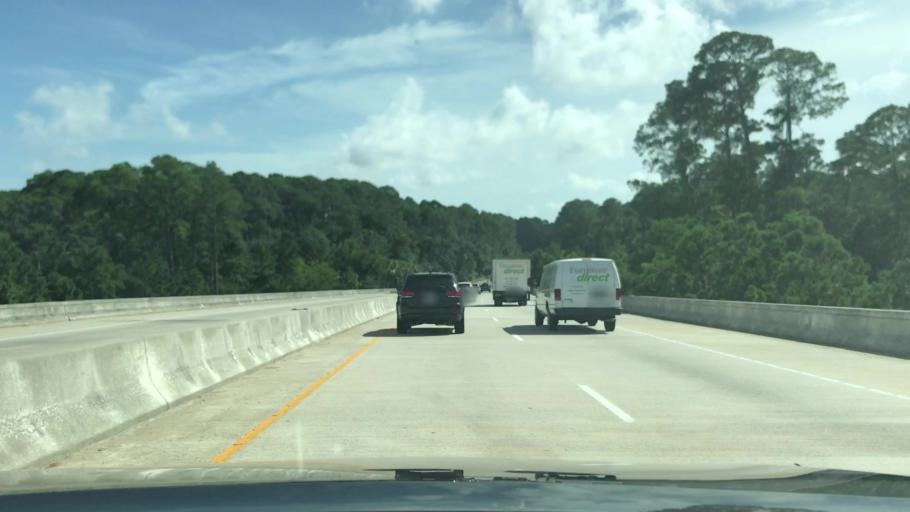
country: US
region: South Carolina
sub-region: Beaufort County
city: Hilton Head Island
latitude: 32.1762
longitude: -80.7702
